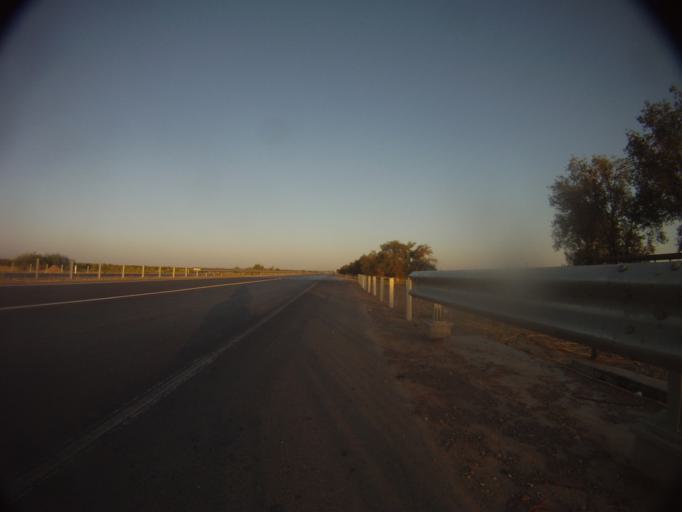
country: KZ
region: Ongtustik Qazaqstan
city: Turkestan
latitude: 43.2701
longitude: 68.3501
